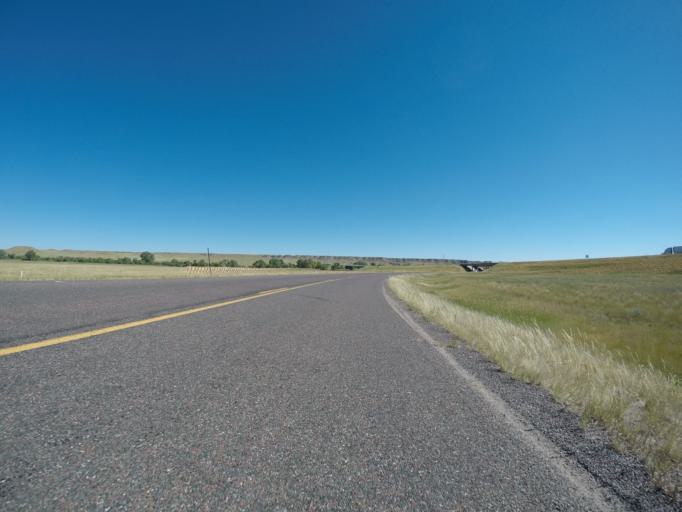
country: US
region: Wyoming
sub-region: Platte County
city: Wheatland
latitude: 41.7452
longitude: -104.8323
